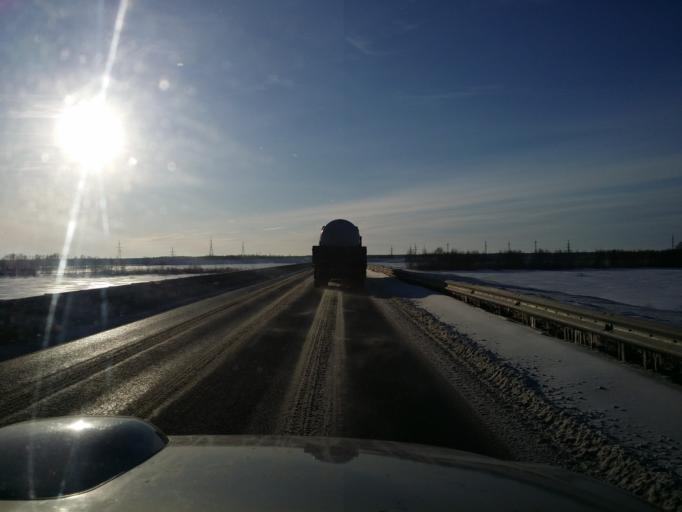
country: RU
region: Khanty-Mansiyskiy Avtonomnyy Okrug
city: Izluchinsk
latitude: 60.9363
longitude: 76.9293
